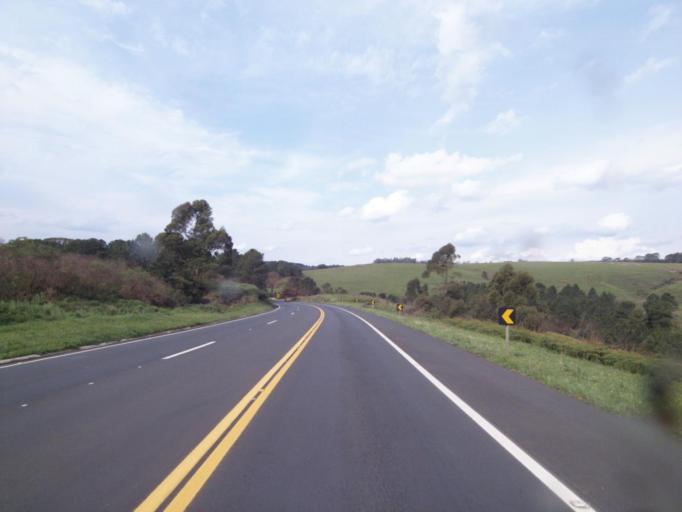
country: BR
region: Parana
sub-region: Campo Largo
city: Campo Largo
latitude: -25.4682
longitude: -49.7697
